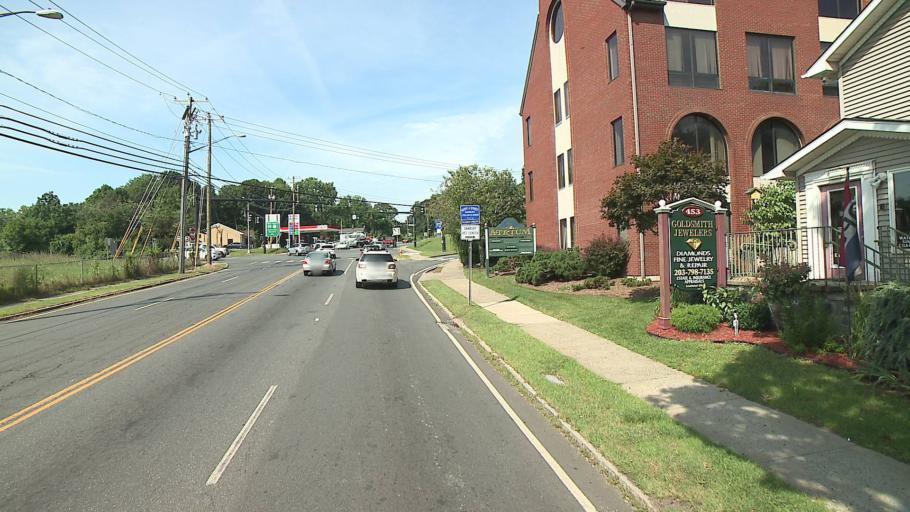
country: US
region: Connecticut
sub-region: Fairfield County
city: Danbury
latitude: 41.4052
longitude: -73.4622
